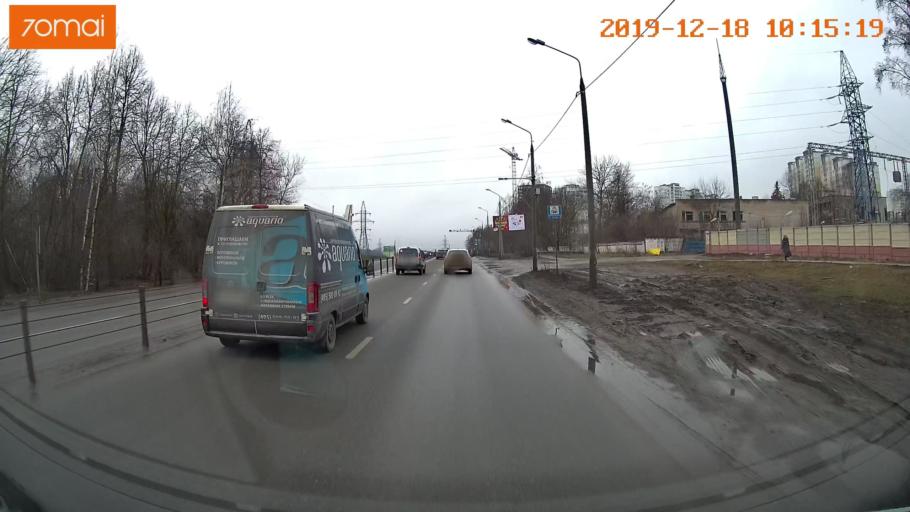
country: RU
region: Moskovskaya
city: Dubrovitsy
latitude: 55.4116
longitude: 37.4822
